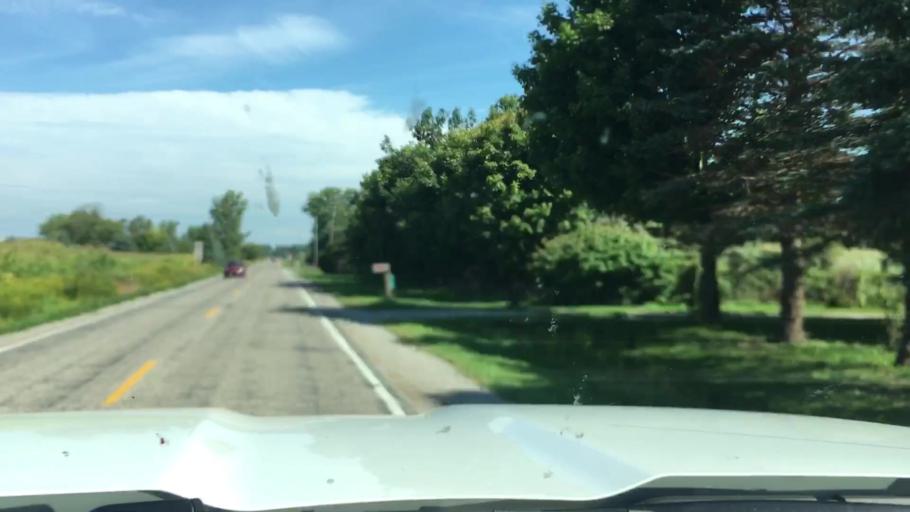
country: US
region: Michigan
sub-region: Saginaw County
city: Hemlock
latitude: 43.4420
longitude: -84.2300
